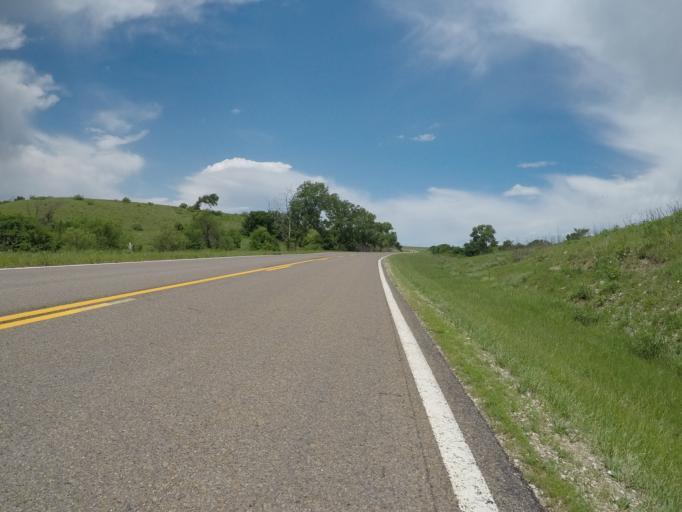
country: US
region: Kansas
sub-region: Wabaunsee County
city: Alma
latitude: 38.8665
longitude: -96.3073
